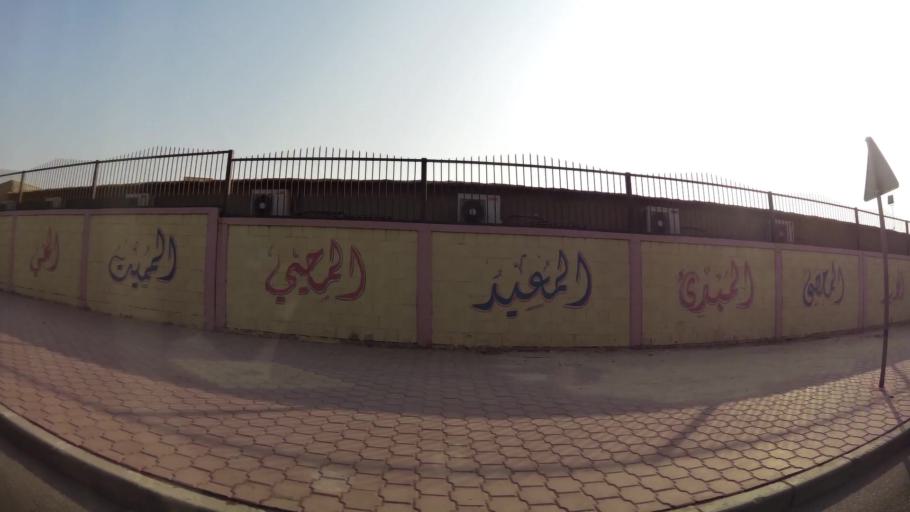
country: KW
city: Bayan
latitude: 29.2930
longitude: 48.0556
